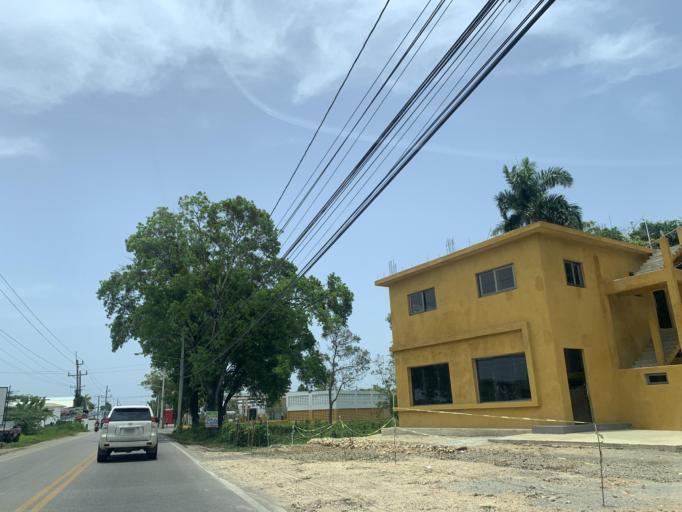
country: DO
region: Puerto Plata
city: Cabarete
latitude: 19.7717
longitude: -70.4990
